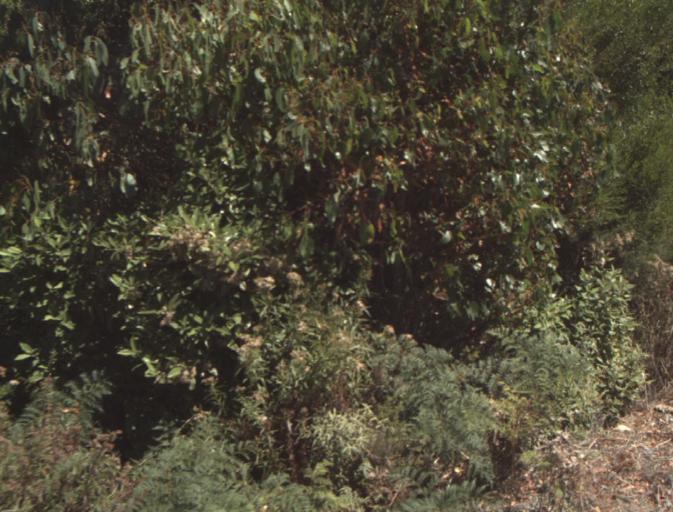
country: AU
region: Tasmania
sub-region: Dorset
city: Scottsdale
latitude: -41.3517
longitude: 147.3868
